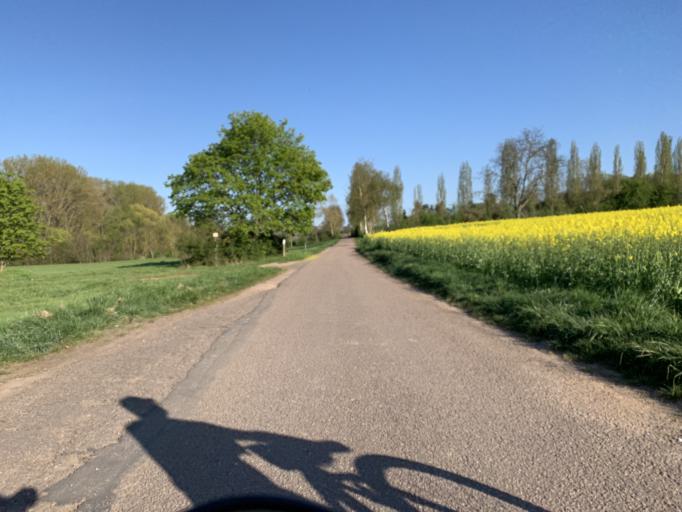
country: DE
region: Rheinland-Pfalz
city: Langenlonsheim
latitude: 49.8876
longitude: 7.8853
